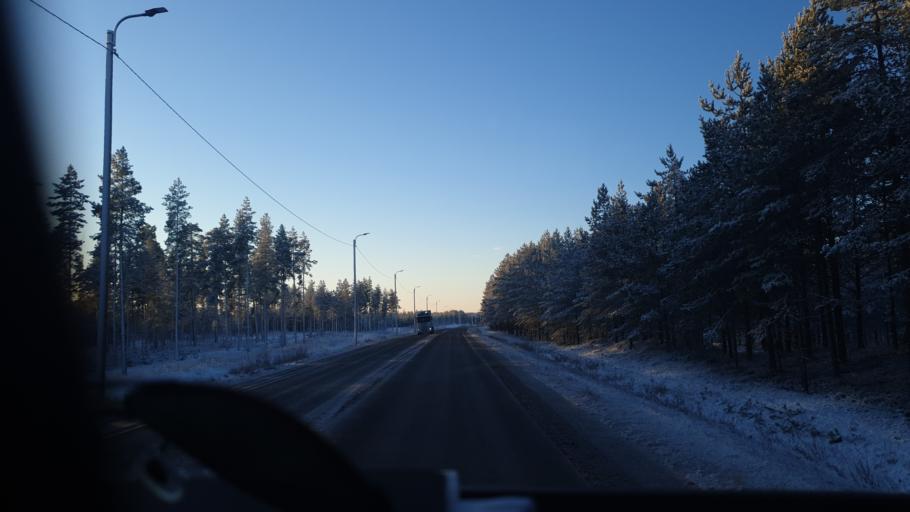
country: FI
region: Northern Ostrobothnia
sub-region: Ylivieska
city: Kalajoki
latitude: 64.2341
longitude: 23.8264
